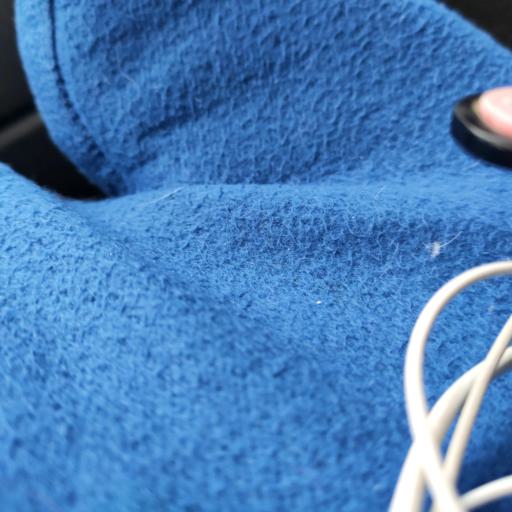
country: RU
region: Bashkortostan
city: Ufa
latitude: 54.8154
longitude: 56.1667
